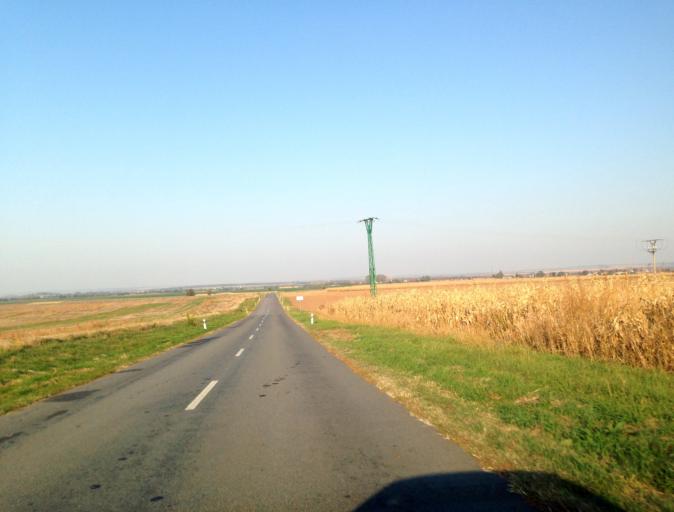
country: SK
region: Nitriansky
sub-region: Okres Komarno
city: Hurbanovo
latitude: 47.9062
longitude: 18.2836
